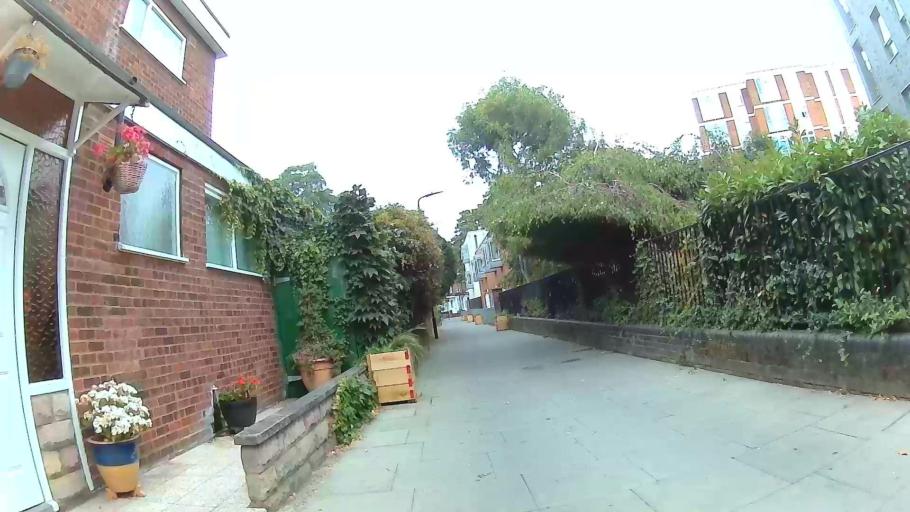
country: GB
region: England
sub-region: Greater London
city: Hackney
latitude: 51.5430
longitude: -0.0530
